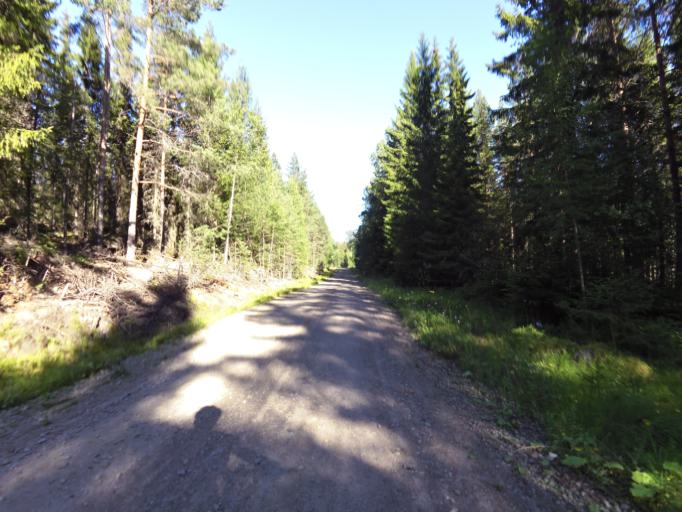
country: SE
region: Gaevleborg
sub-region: Hofors Kommun
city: Hofors
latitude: 60.6518
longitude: 16.2530
